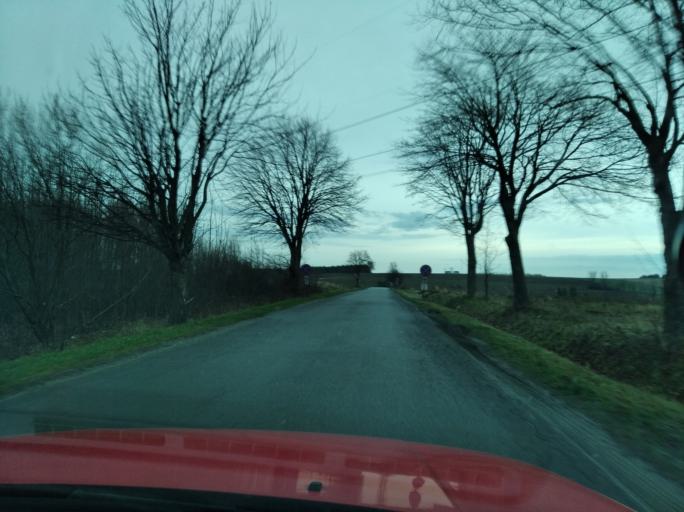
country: PL
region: Subcarpathian Voivodeship
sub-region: Powiat strzyzowski
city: Jawornik
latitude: 49.8738
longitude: 21.8574
